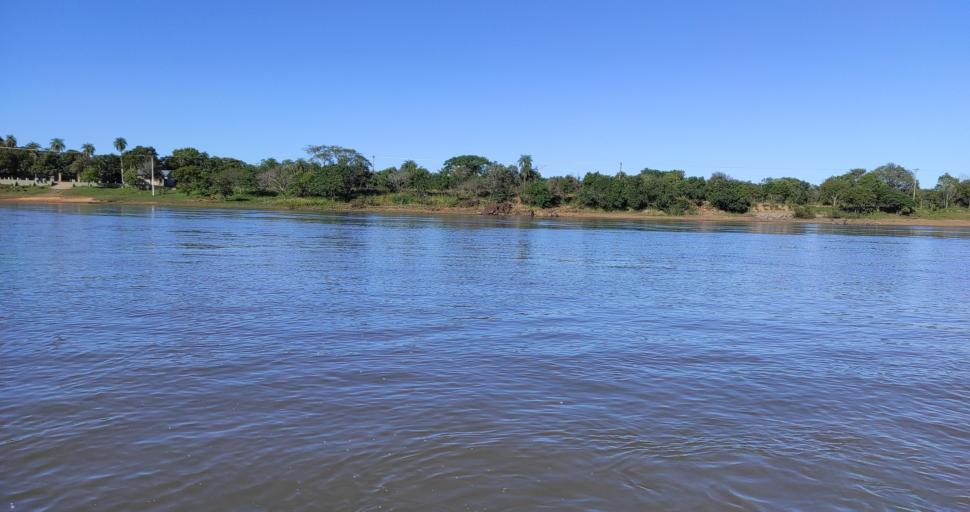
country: AR
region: Corrientes
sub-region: Departamento de Itati
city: Itati
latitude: -27.2636
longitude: -58.2584
